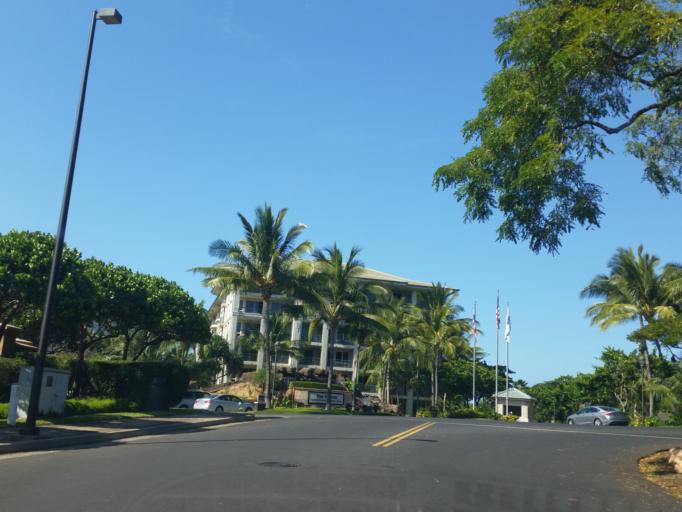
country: US
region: Hawaii
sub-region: Maui County
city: Kaanapali Landing
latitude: 20.9359
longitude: -156.6913
